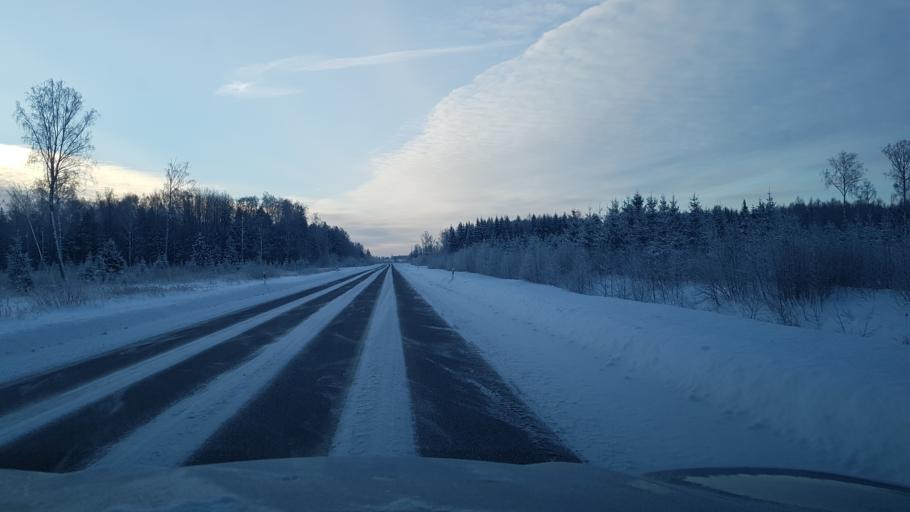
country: EE
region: Ida-Virumaa
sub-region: Johvi vald
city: Johvi
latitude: 59.3498
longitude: 27.4676
